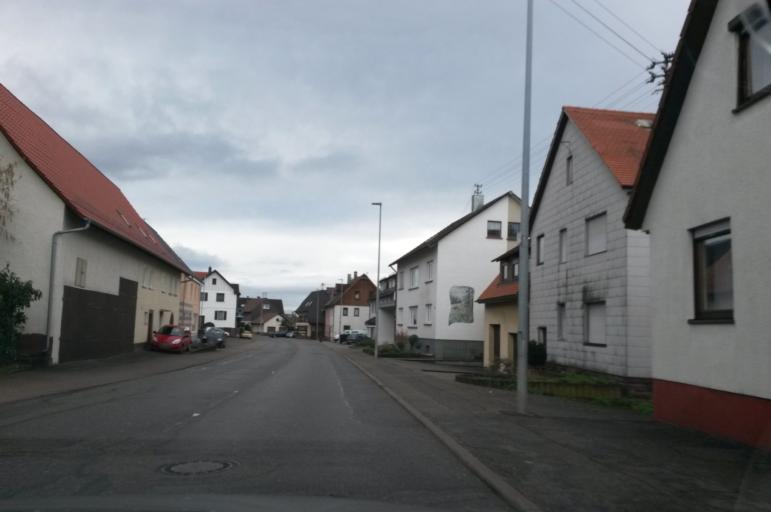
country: DE
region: Baden-Wuerttemberg
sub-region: Karlsruhe Region
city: Dobel
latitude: 48.8426
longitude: 8.5337
